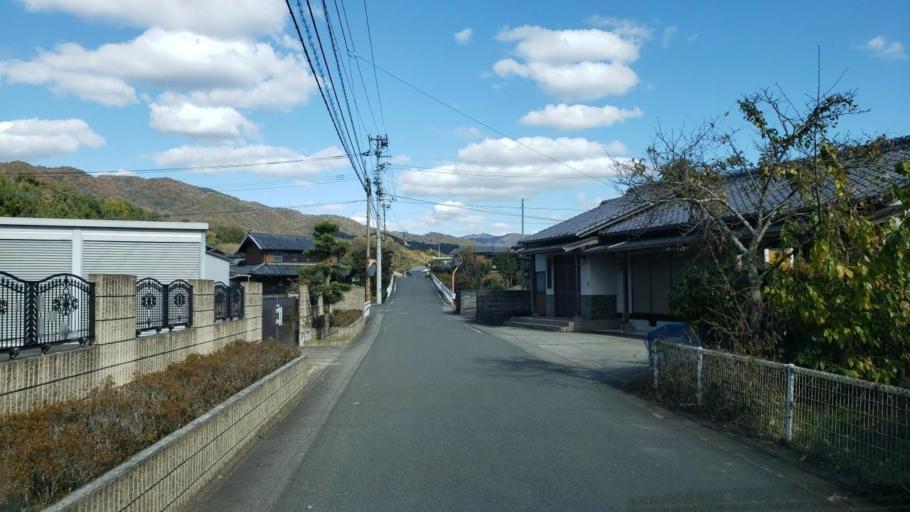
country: JP
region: Tokushima
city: Wakimachi
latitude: 34.0768
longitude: 134.1945
